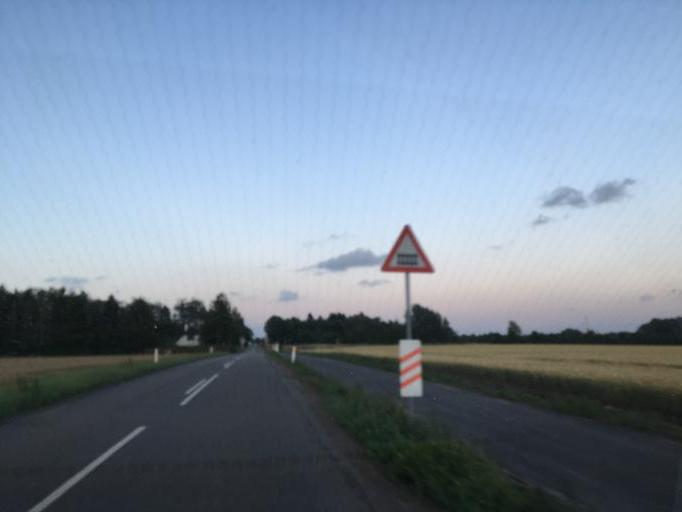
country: DK
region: Zealand
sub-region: Solrod Kommune
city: Havdrup
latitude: 55.5216
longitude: 12.1277
